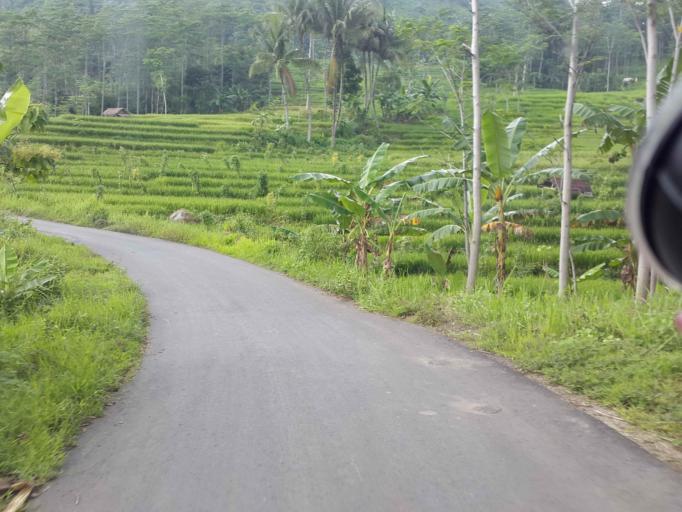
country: ID
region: Central Java
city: Buaran
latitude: -7.1203
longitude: 109.4897
